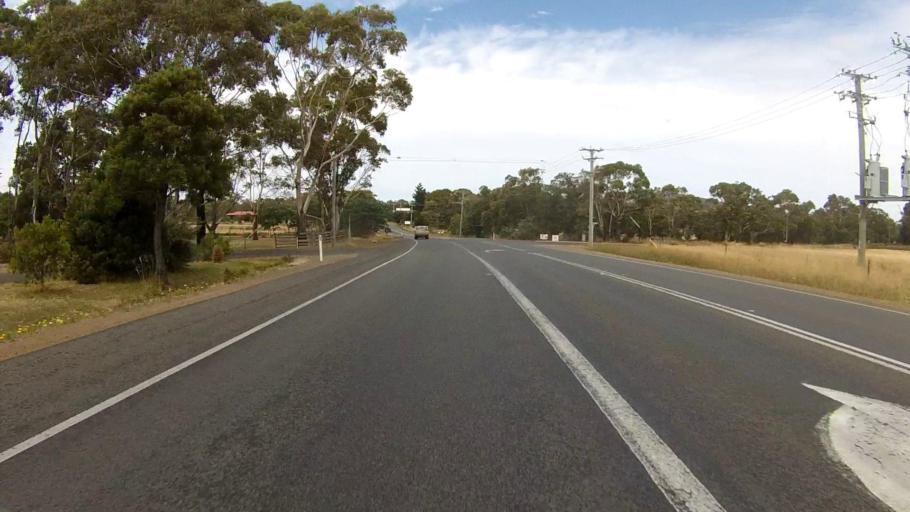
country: AU
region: Tasmania
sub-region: Clarence
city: Sandford
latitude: -42.9346
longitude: 147.4922
